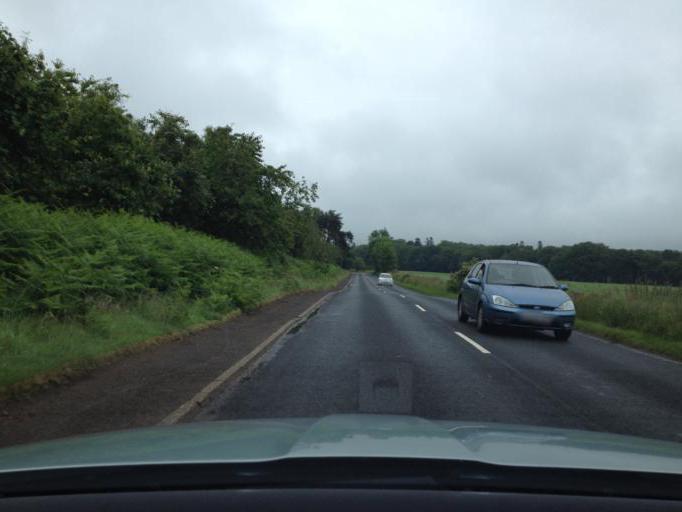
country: GB
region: Scotland
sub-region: Angus
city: Brechin
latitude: 56.8219
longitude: -2.6580
